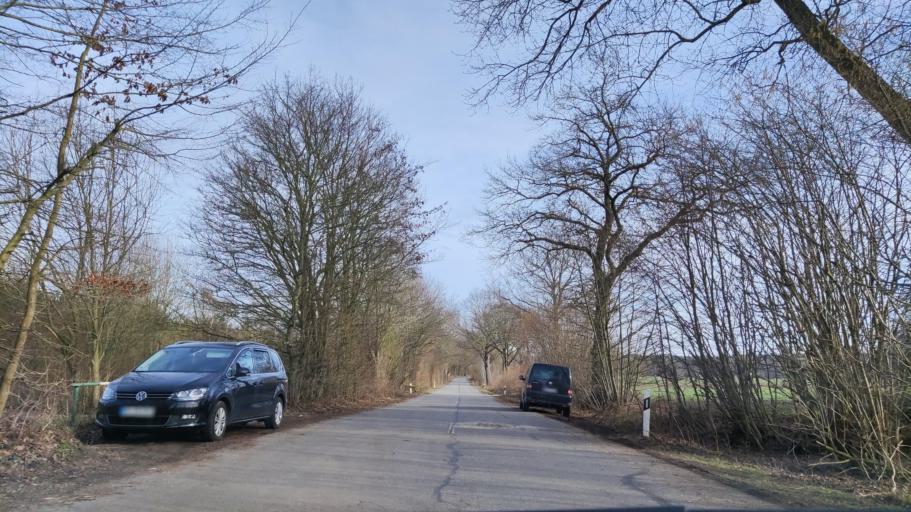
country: DE
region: Schleswig-Holstein
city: Schackendorf
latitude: 53.9696
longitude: 10.2633
